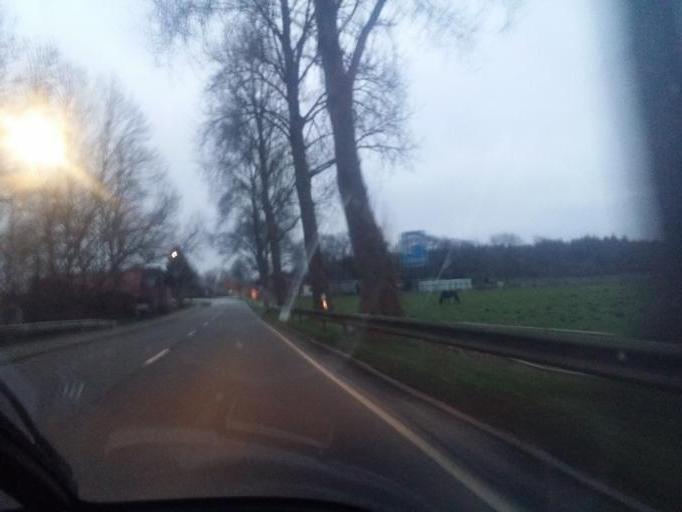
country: DE
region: Schleswig-Holstein
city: Gokels
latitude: 54.1191
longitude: 9.4471
